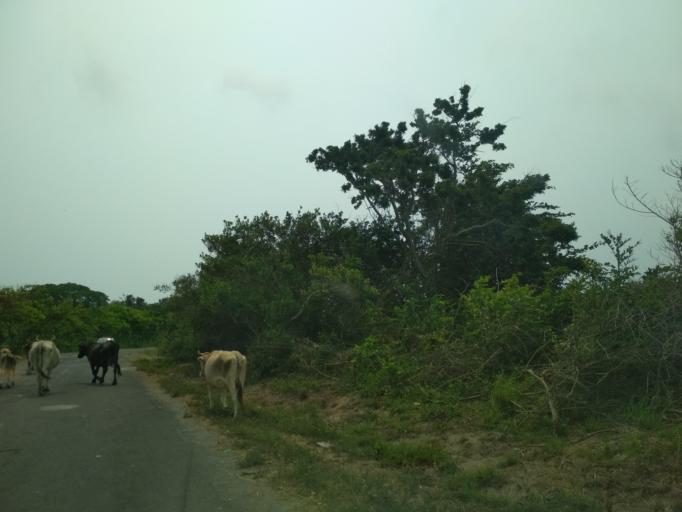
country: MX
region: Veracruz
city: Anton Lizardo
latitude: 19.0388
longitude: -95.9789
